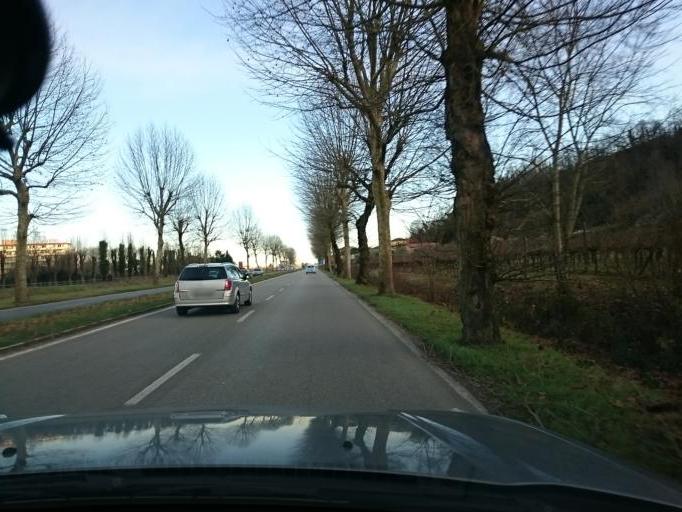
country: IT
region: Veneto
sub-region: Provincia di Padova
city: Montegrotto Terme
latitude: 45.3226
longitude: 11.7805
